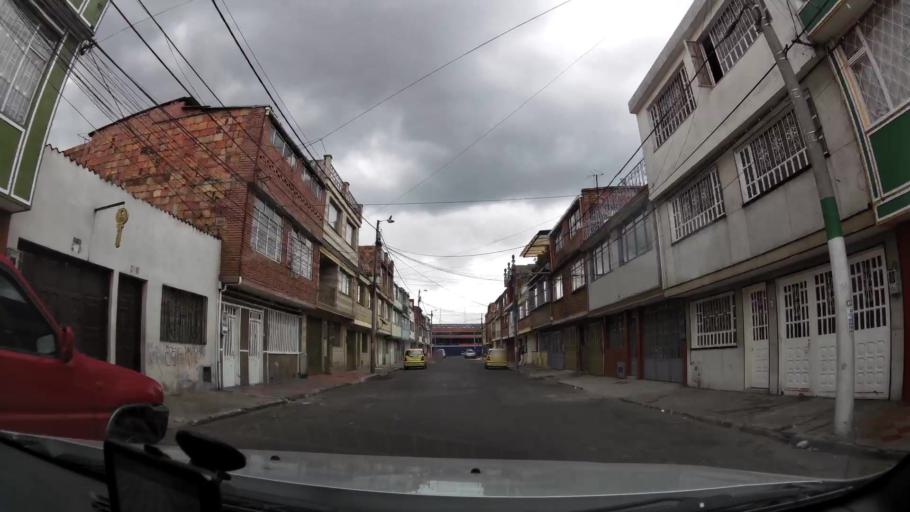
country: CO
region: Bogota D.C.
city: Bogota
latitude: 4.6217
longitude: -74.1119
